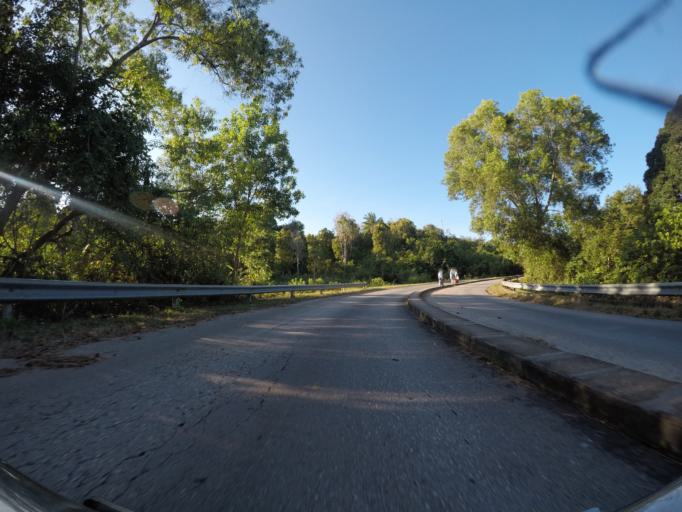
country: TZ
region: Pemba South
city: Uwelini
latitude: -5.3768
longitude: 39.6737
